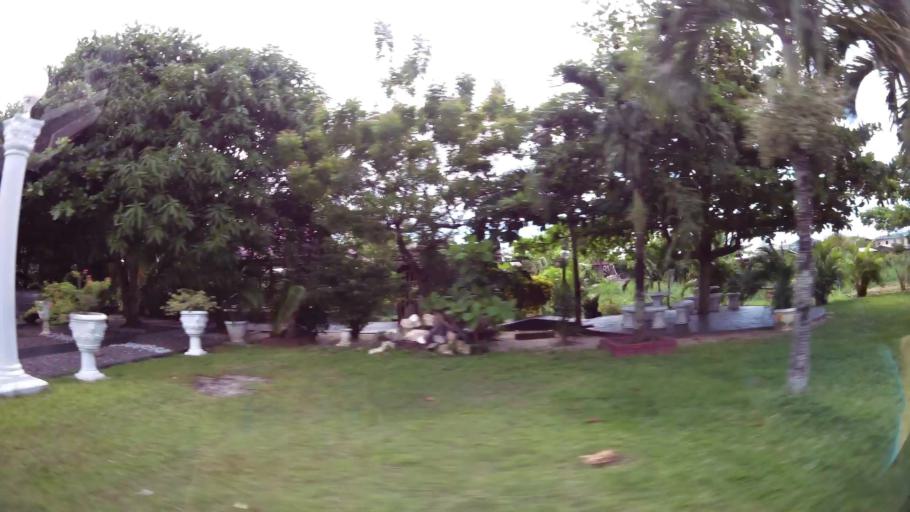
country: SR
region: Paramaribo
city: Paramaribo
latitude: 5.8487
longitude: -55.1515
